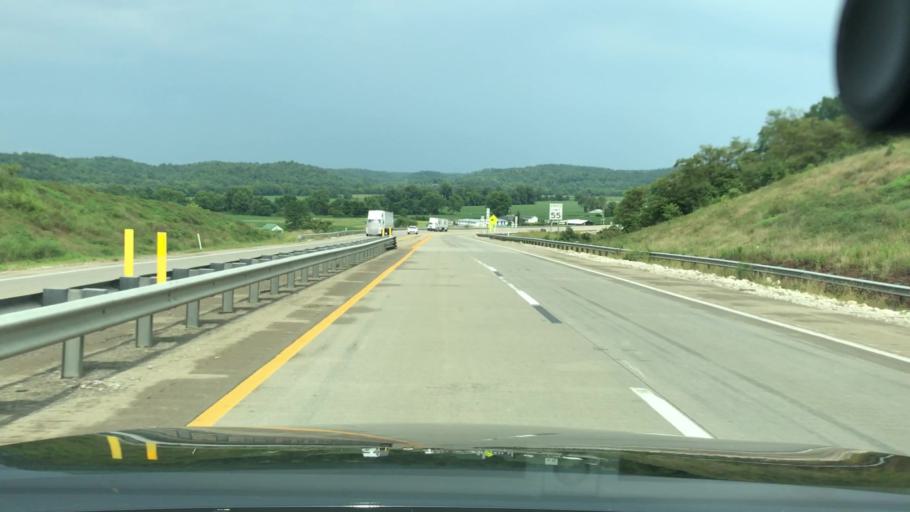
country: US
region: West Virginia
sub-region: Mason County
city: Point Pleasant
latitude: 38.7657
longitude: -82.0116
